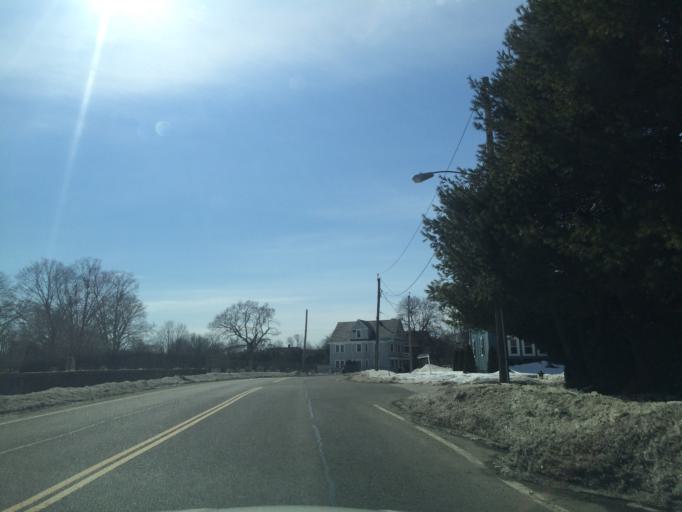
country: US
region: Massachusetts
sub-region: Middlesex County
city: Belmont
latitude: 42.3809
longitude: -71.1579
